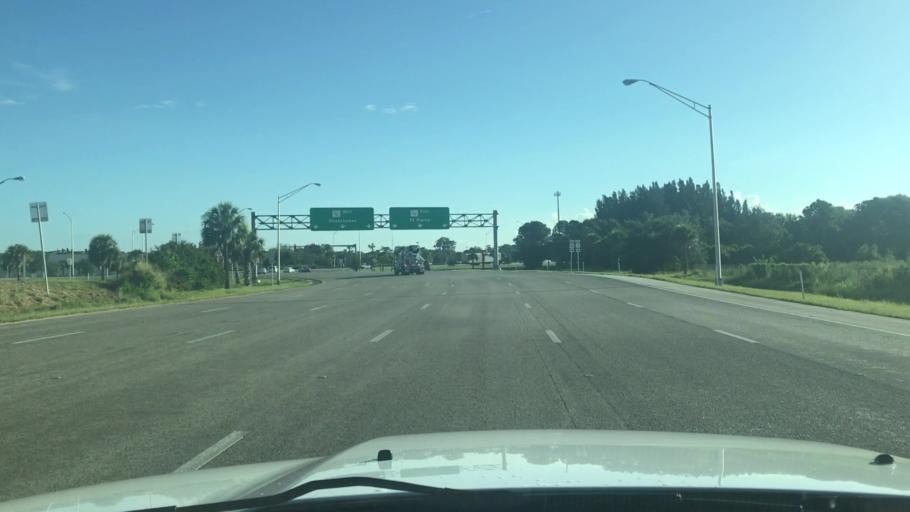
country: US
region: Florida
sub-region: Saint Lucie County
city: Fort Pierce South
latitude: 27.4145
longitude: -80.3865
